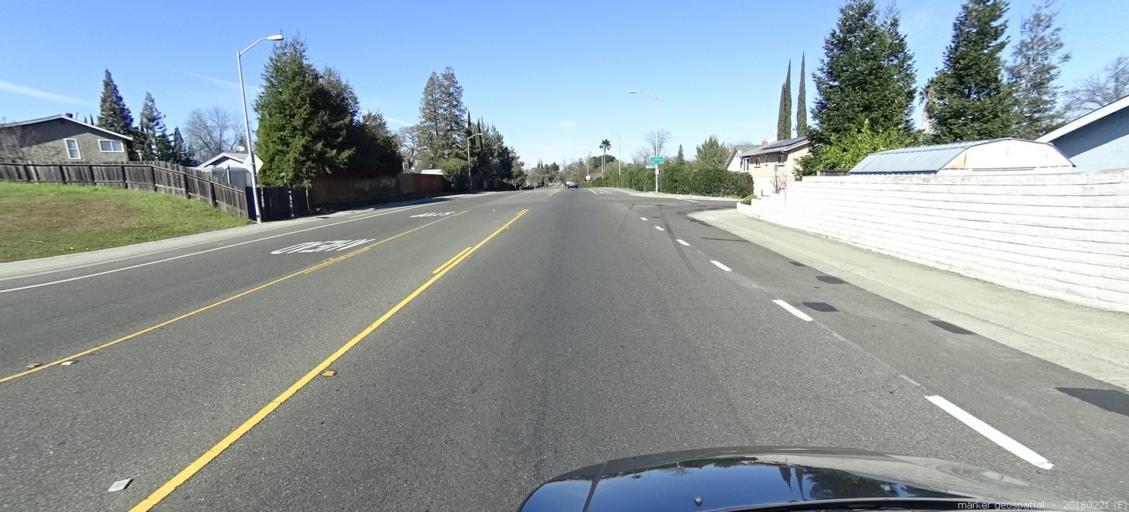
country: US
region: California
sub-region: Sacramento County
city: Citrus Heights
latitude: 38.6932
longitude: -121.2623
